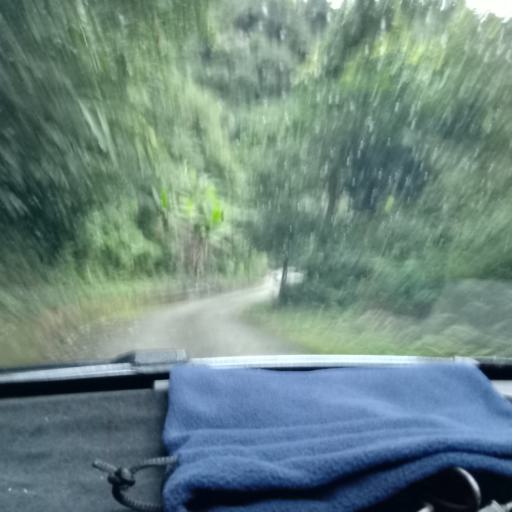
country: TW
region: Taiwan
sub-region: Yilan
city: Yilan
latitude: 24.8093
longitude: 121.6982
